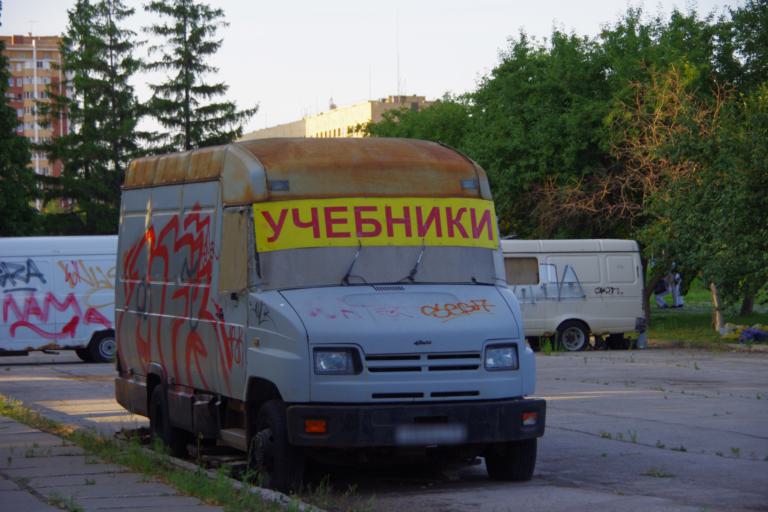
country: RU
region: Samara
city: Tol'yatti
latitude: 53.5227
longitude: 49.2748
